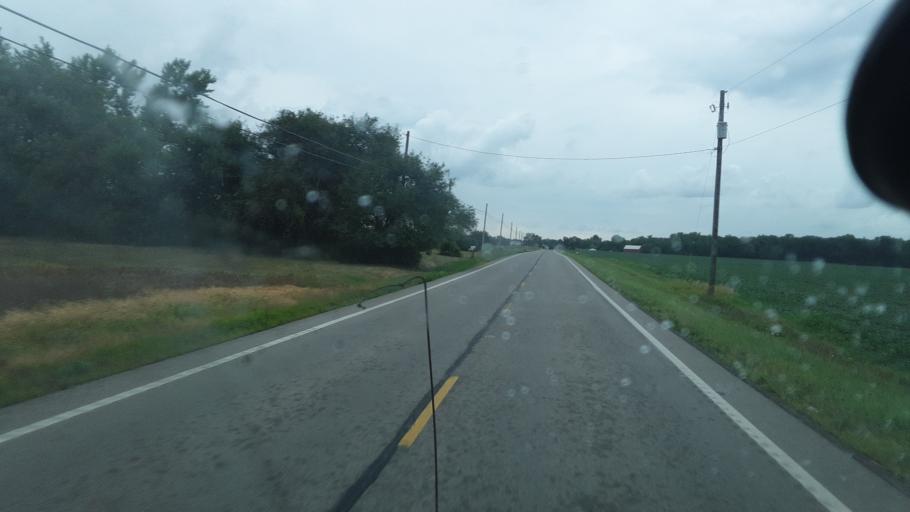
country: US
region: Ohio
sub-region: Williams County
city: Bryan
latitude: 41.4345
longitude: -84.6044
